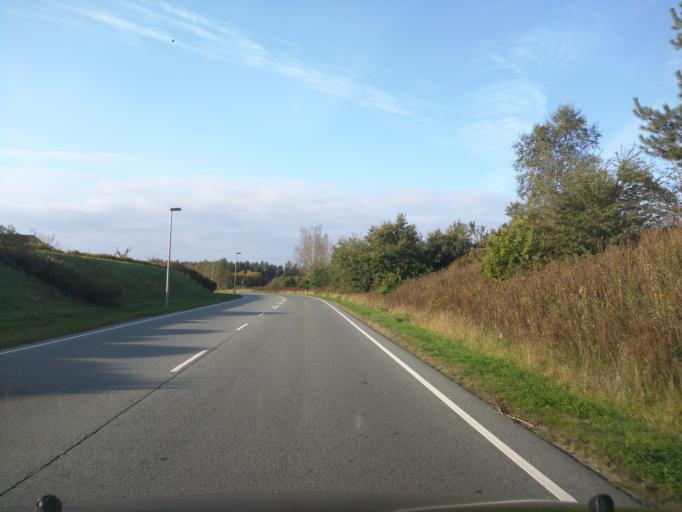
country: DK
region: Central Jutland
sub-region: Viborg Kommune
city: Viborg
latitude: 56.4672
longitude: 9.3785
